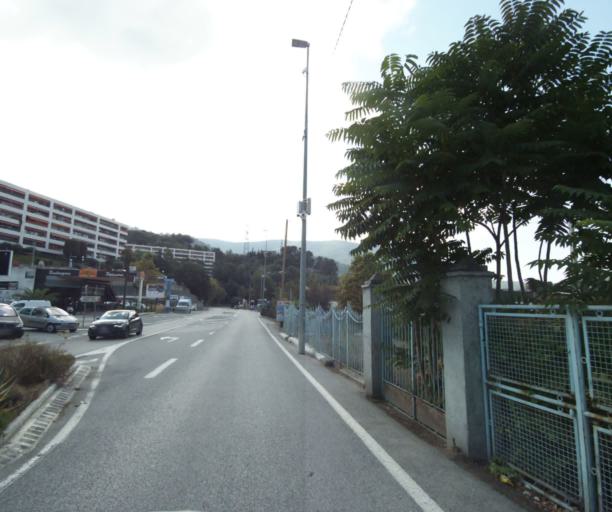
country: FR
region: Provence-Alpes-Cote d'Azur
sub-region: Departement des Alpes-Maritimes
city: Drap
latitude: 43.7499
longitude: 7.3199
